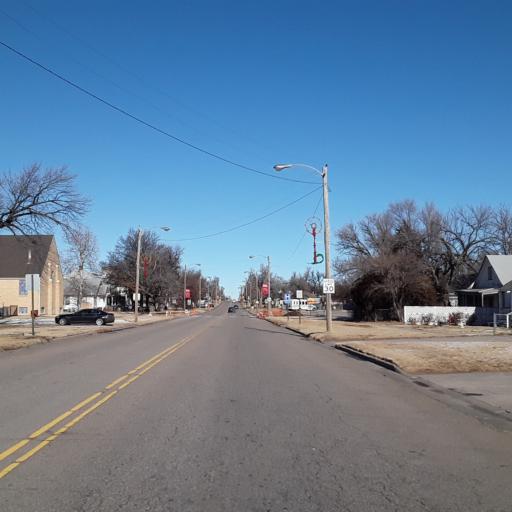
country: US
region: Kansas
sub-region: Pawnee County
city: Larned
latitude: 38.1844
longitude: -99.0984
